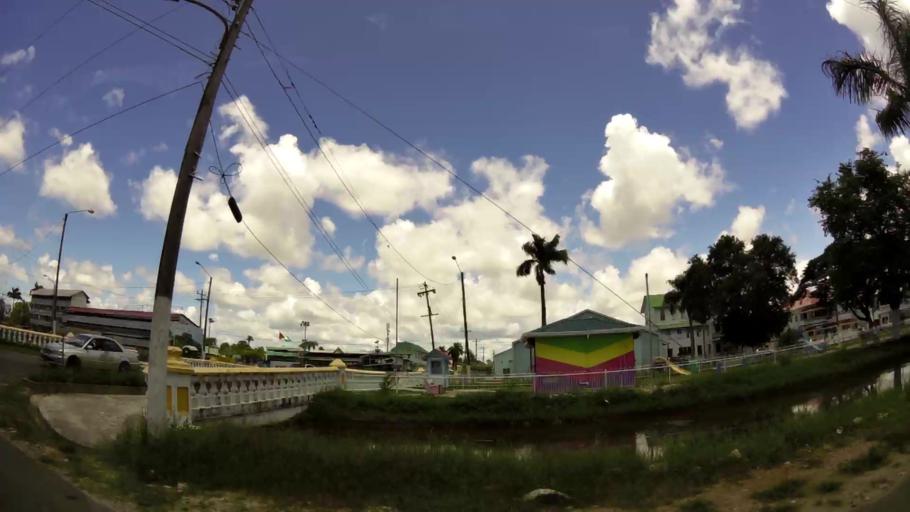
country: GY
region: Demerara-Mahaica
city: Georgetown
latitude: 6.8096
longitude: -58.1504
